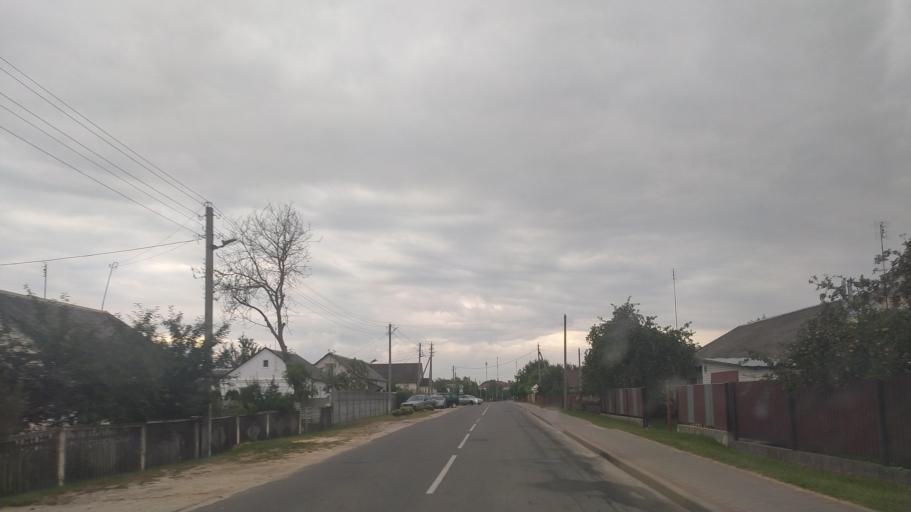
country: BY
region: Brest
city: Byaroza
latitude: 52.5230
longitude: 24.9730
